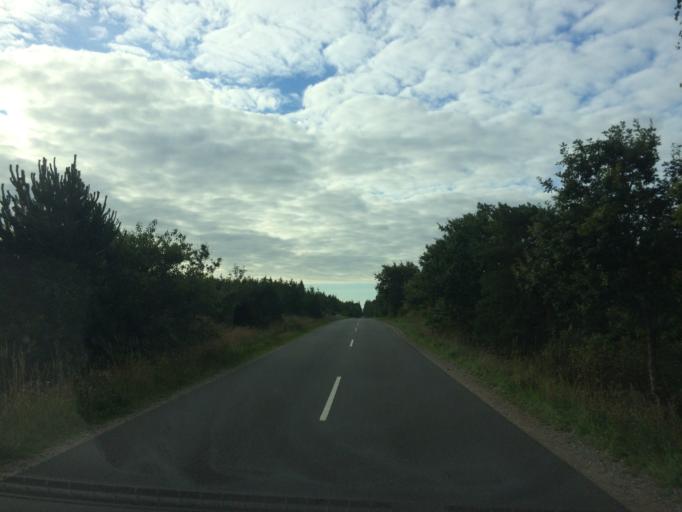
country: DK
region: Central Jutland
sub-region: Holstebro Kommune
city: Ulfborg
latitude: 56.2164
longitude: 8.3907
